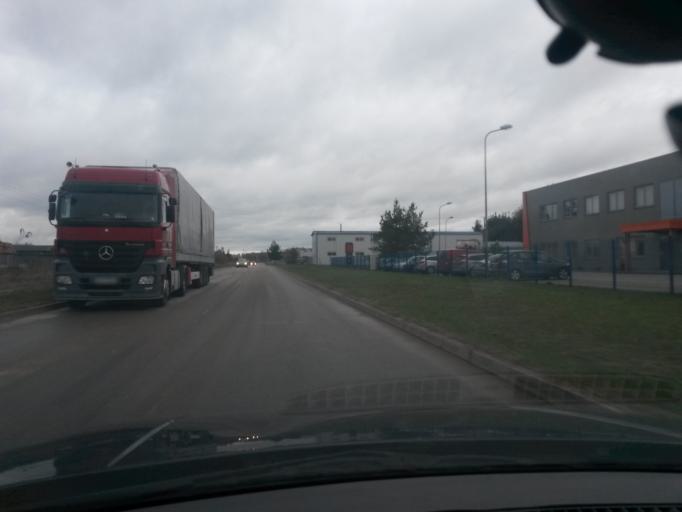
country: LV
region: Stopini
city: Ulbroka
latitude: 56.9084
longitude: 24.2461
